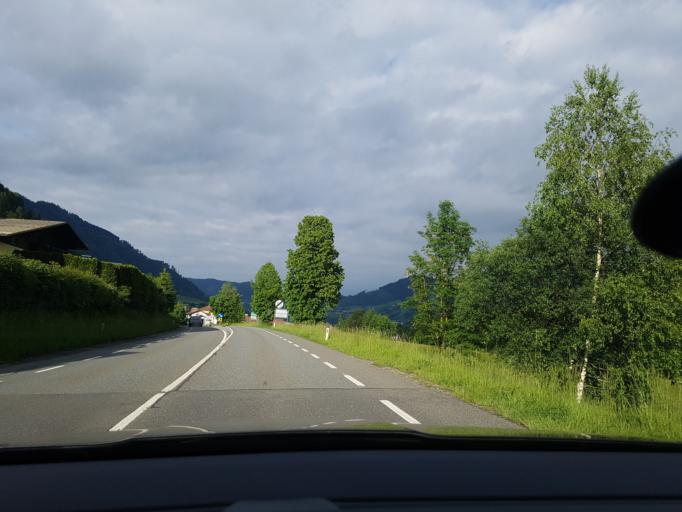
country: AT
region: Salzburg
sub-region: Politischer Bezirk Sankt Johann im Pongau
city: Schwarzach im Pongau
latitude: 47.3173
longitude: 13.1371
